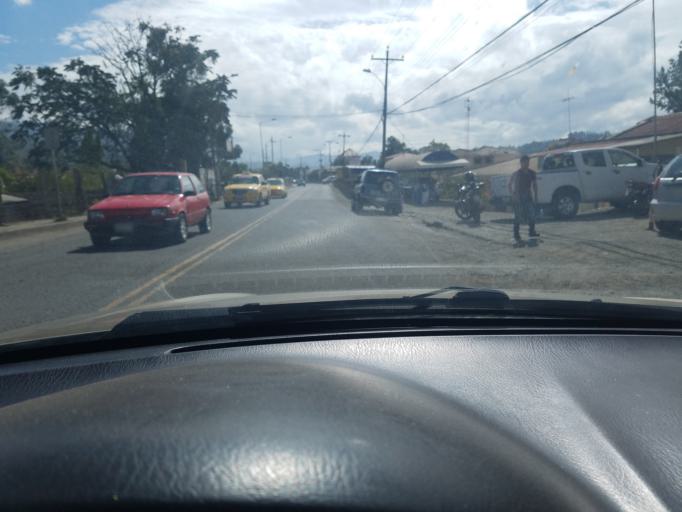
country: EC
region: Azuay
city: Llacao
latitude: -2.8623
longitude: -78.9363
